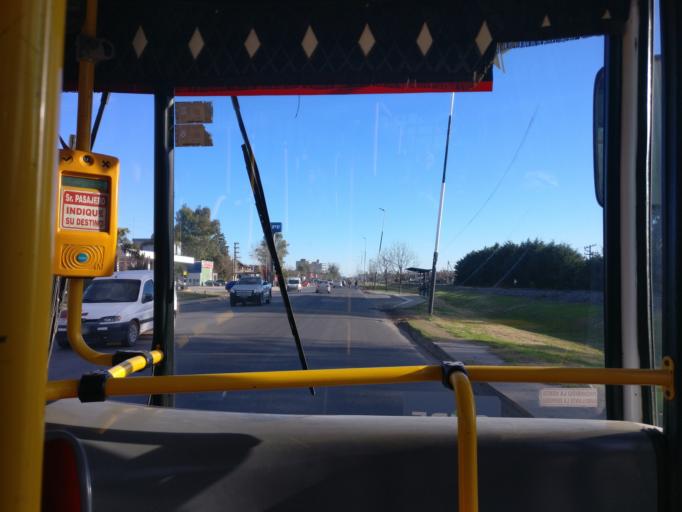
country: AR
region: Buenos Aires
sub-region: Partido de Ezeiza
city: Ezeiza
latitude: -34.8772
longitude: -58.5520
